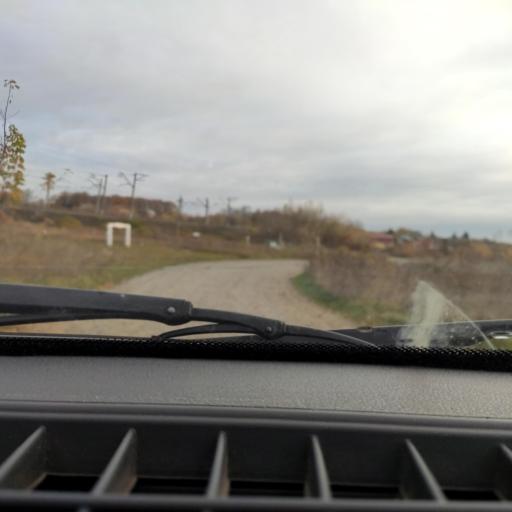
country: RU
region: Bashkortostan
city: Avdon
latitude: 54.6372
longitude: 55.7275
